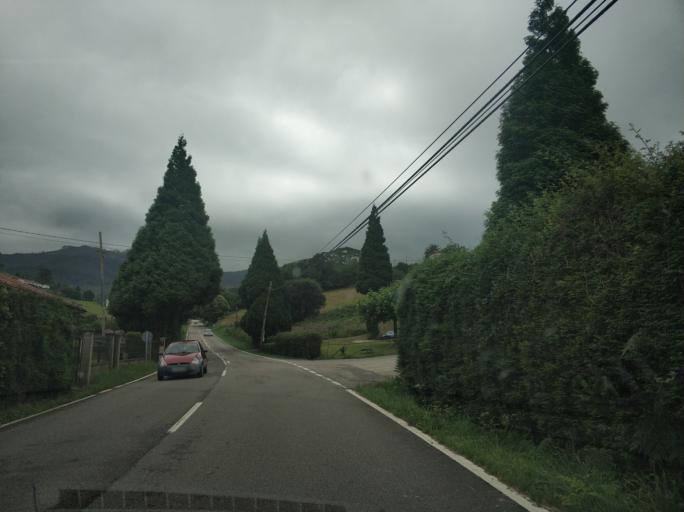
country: ES
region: Asturias
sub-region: Province of Asturias
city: Cudillero
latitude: 43.5510
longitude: -6.2257
